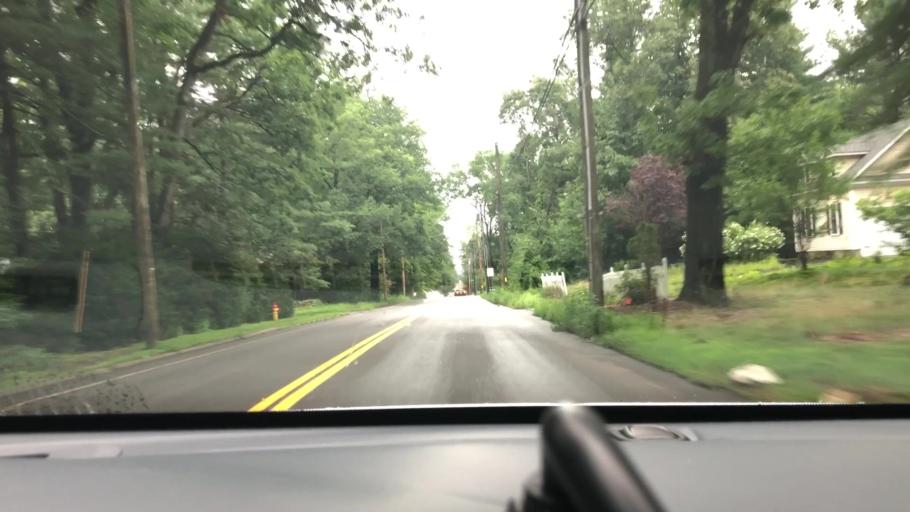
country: US
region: New Hampshire
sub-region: Hillsborough County
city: Manchester
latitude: 43.0216
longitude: -71.4623
